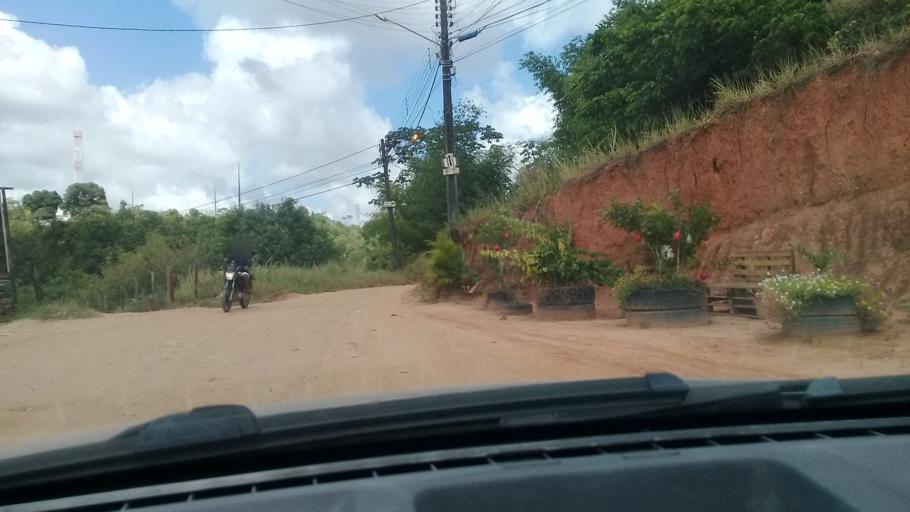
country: BR
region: Pernambuco
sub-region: Jaboatao Dos Guararapes
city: Jaboatao dos Guararapes
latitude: -8.0903
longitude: -35.0289
